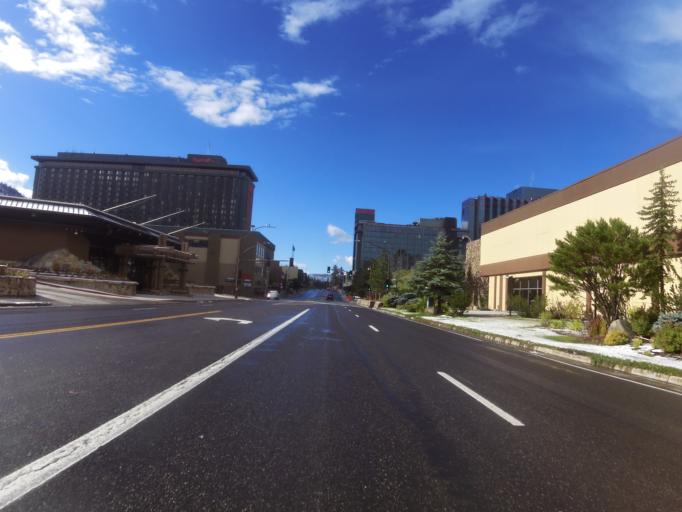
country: US
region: Nevada
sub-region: Douglas County
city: Kingsbury
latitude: 38.9622
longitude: -119.9401
